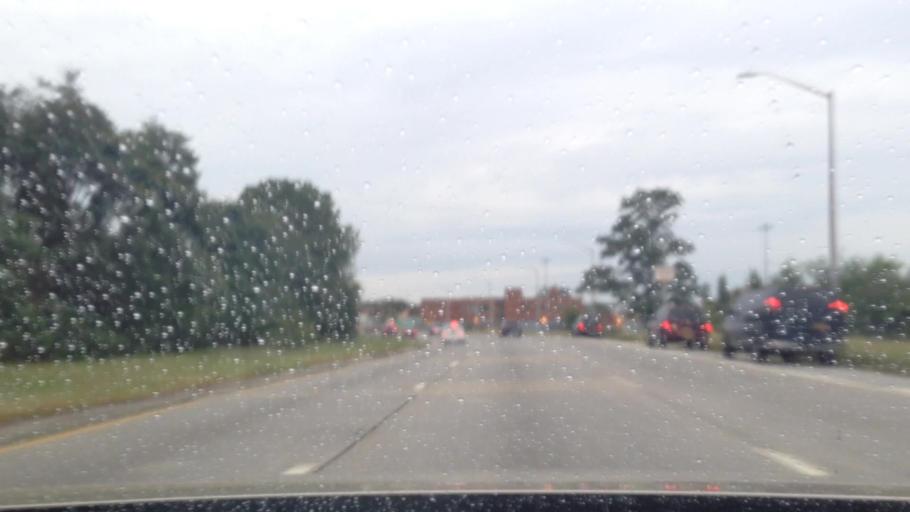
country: US
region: New York
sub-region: Queens County
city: Borough of Queens
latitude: 40.6629
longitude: -73.8152
